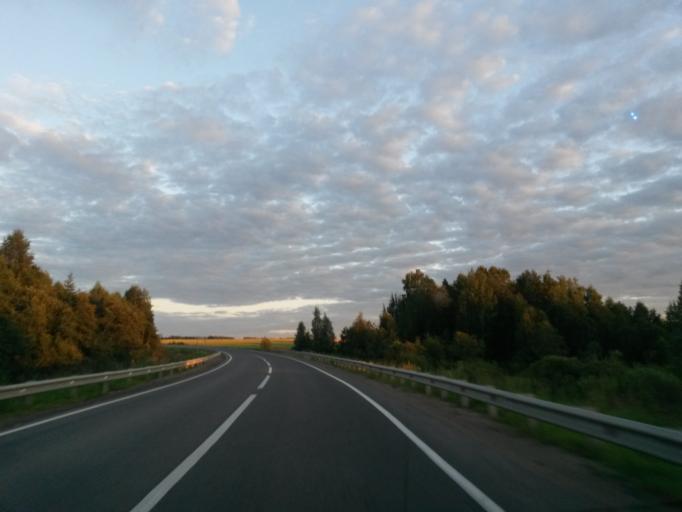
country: RU
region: Jaroslavl
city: Gavrilov-Yam
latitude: 57.3289
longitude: 39.9214
